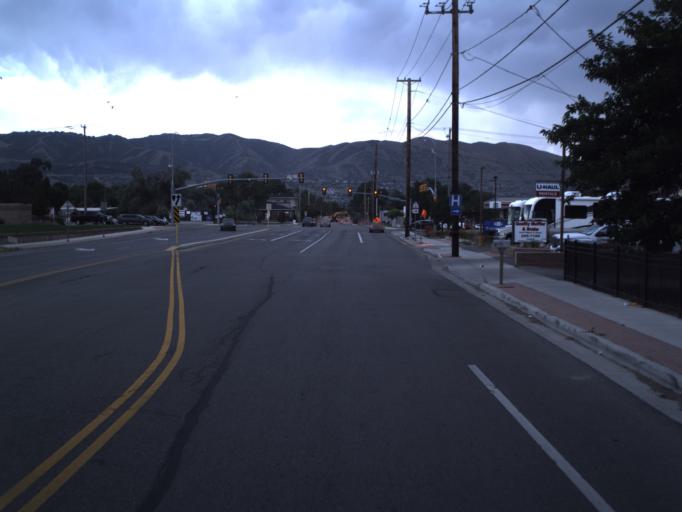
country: US
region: Utah
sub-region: Salt Lake County
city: Draper
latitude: 40.5282
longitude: -111.8713
